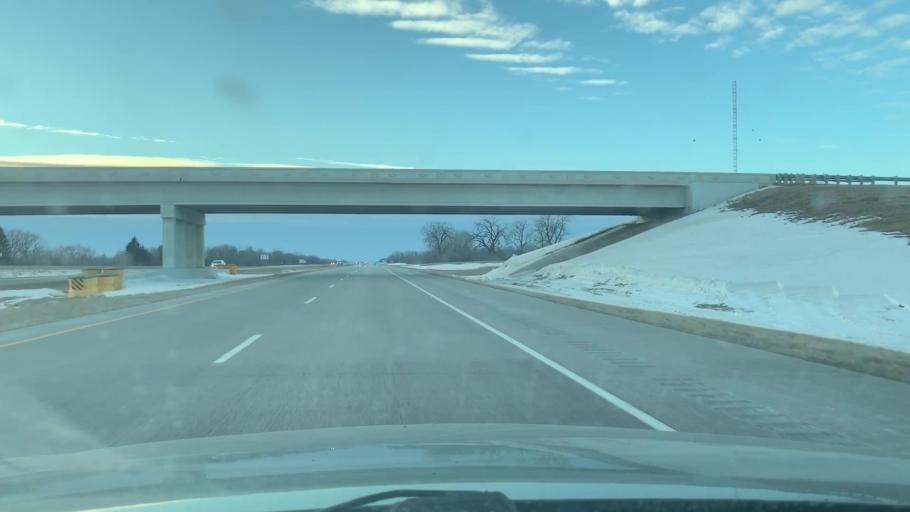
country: US
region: North Dakota
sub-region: Cass County
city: Casselton
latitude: 46.8766
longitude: -97.4303
